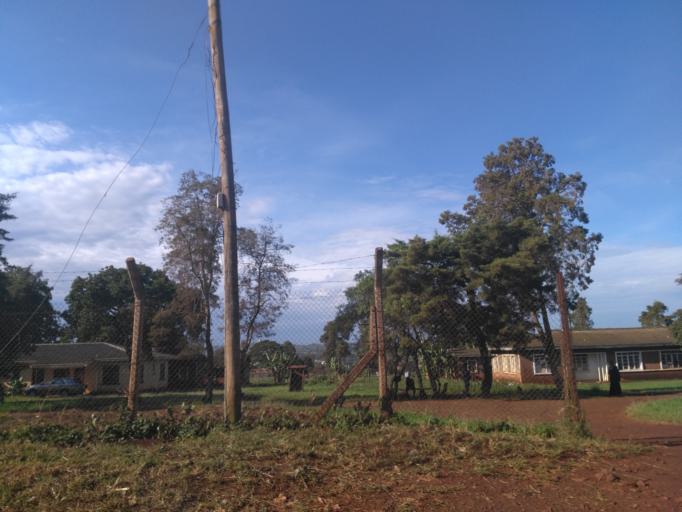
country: UG
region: Eastern Region
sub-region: Jinja District
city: Jinja
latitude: 0.4504
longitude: 33.1932
